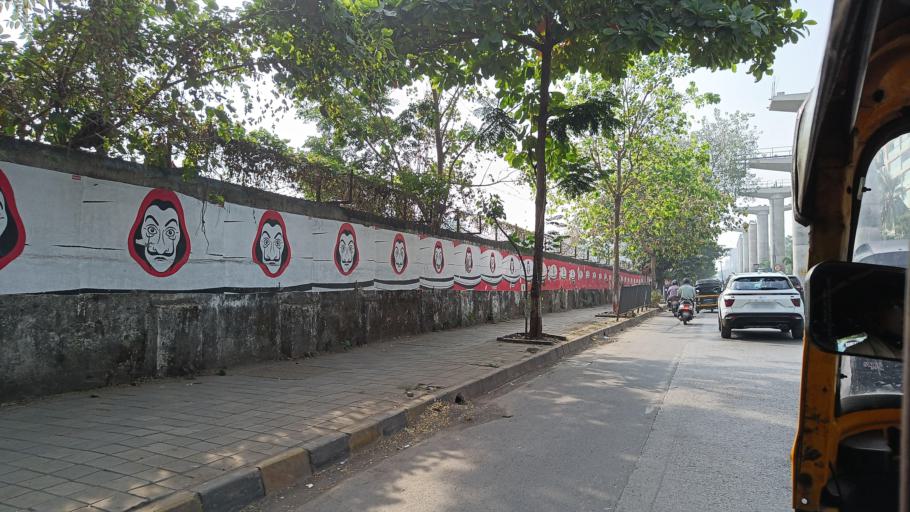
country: IN
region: Maharashtra
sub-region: Mumbai Suburban
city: Mumbai
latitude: 19.1206
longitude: 72.8299
